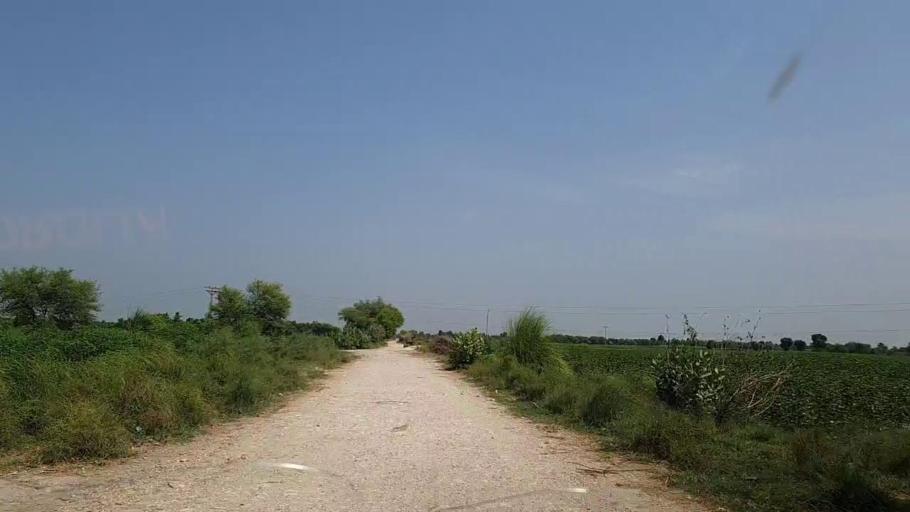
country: PK
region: Sindh
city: Adilpur
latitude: 27.8386
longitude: 69.2793
